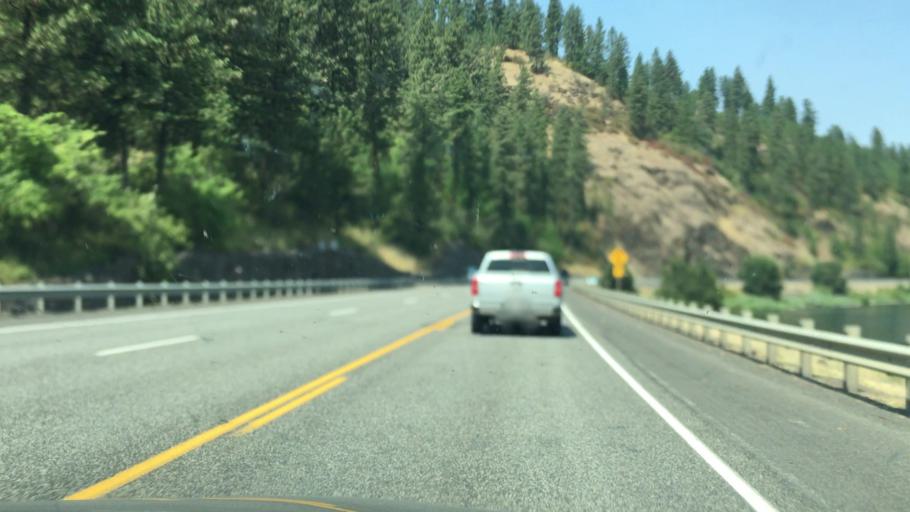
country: US
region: Idaho
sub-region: Nez Perce County
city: Lapwai
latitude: 46.5064
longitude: -116.5748
